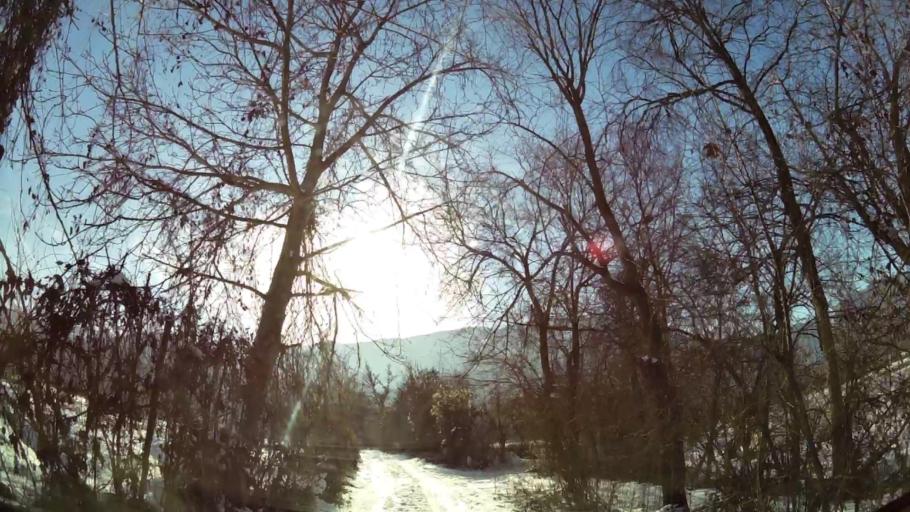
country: MK
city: Grchec
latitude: 41.9840
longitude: 21.3239
